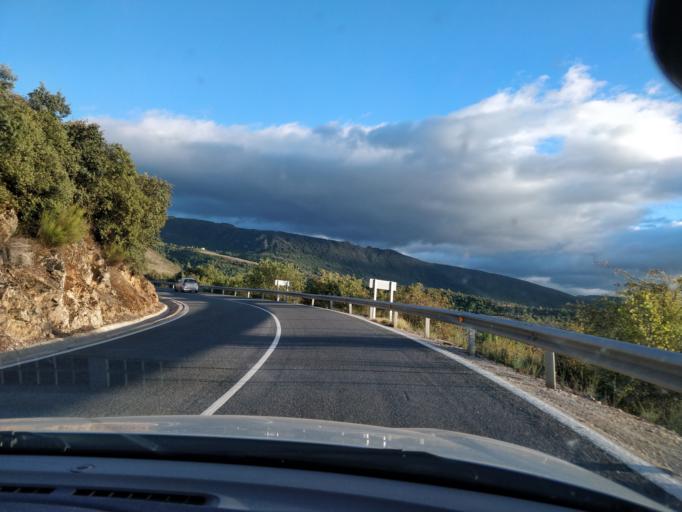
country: ES
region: Castille and Leon
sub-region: Provincia de Leon
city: Borrenes
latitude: 42.4972
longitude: -6.7193
